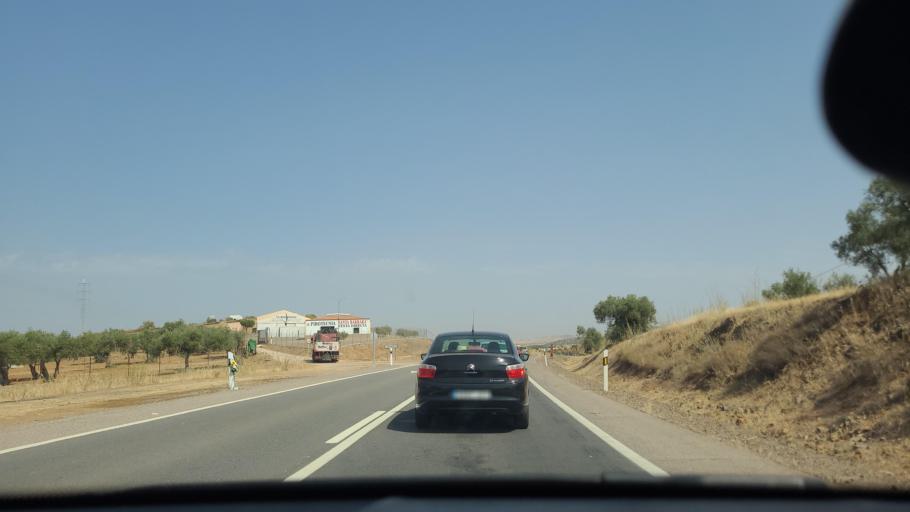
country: ES
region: Extremadura
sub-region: Provincia de Badajoz
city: Zafra
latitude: 38.4432
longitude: -6.4253
